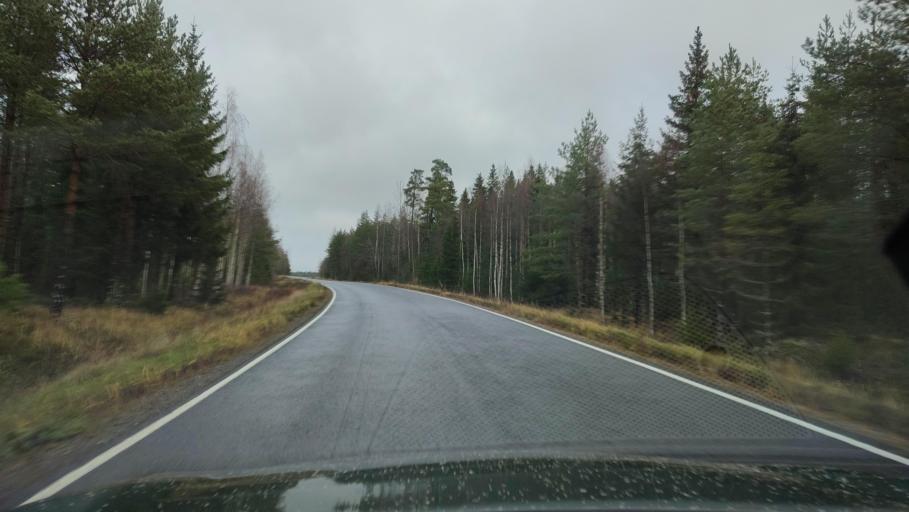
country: FI
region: Ostrobothnia
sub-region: Sydosterbotten
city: Kristinestad
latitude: 62.3351
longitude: 21.5136
